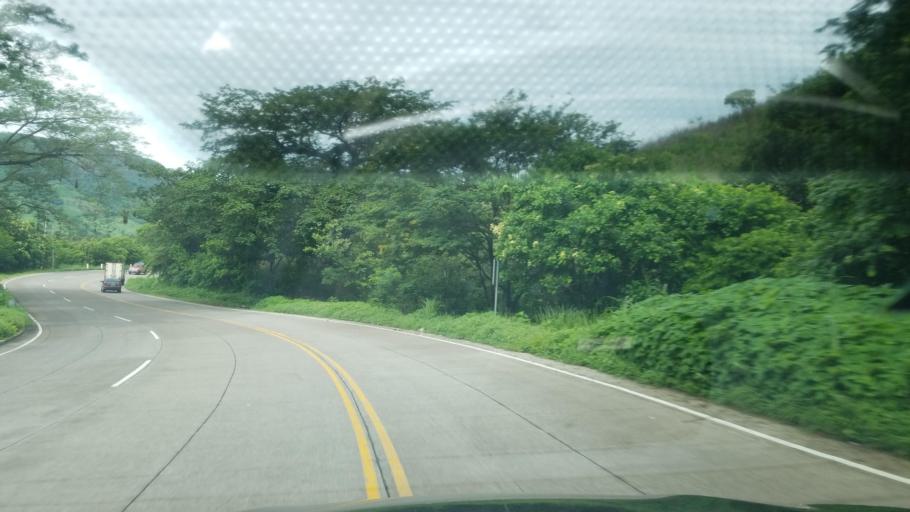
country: HN
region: Francisco Morazan
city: El Porvenir
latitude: 13.6998
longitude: -87.3217
